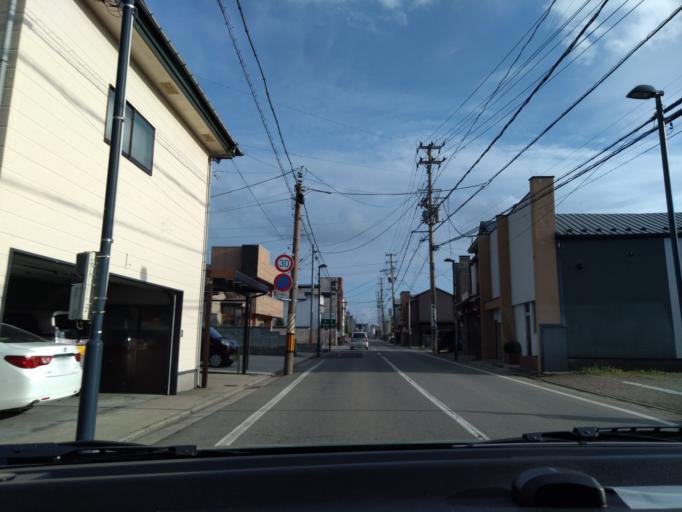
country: JP
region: Akita
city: Akita Shi
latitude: 39.7603
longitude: 140.0693
